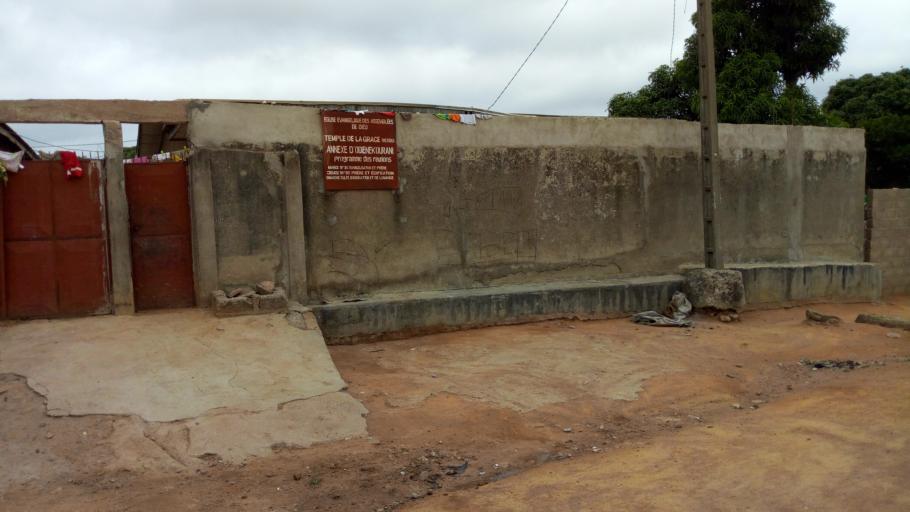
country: CI
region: Vallee du Bandama
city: Bouake
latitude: 7.7016
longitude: -5.0406
